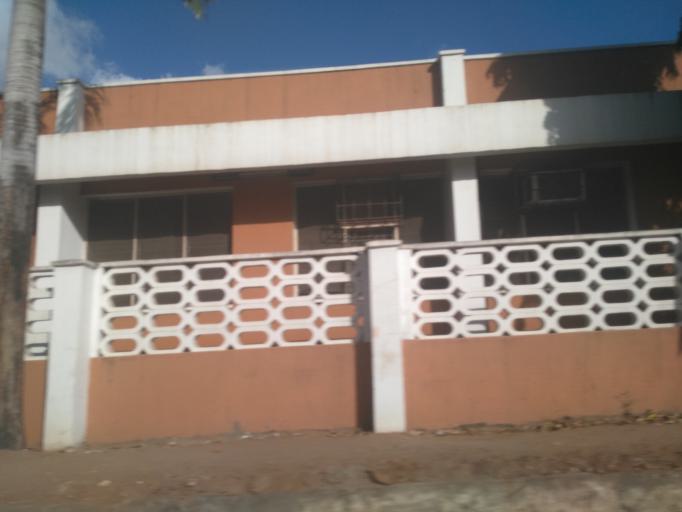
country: TZ
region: Dar es Salaam
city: Dar es Salaam
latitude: -6.8635
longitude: 39.2602
